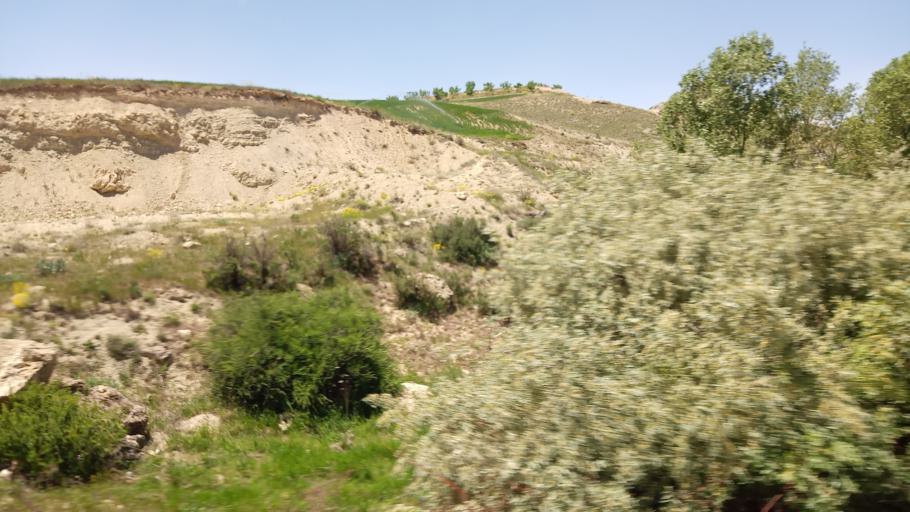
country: TR
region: Sivas
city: Gurun
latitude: 38.6905
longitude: 37.4244
